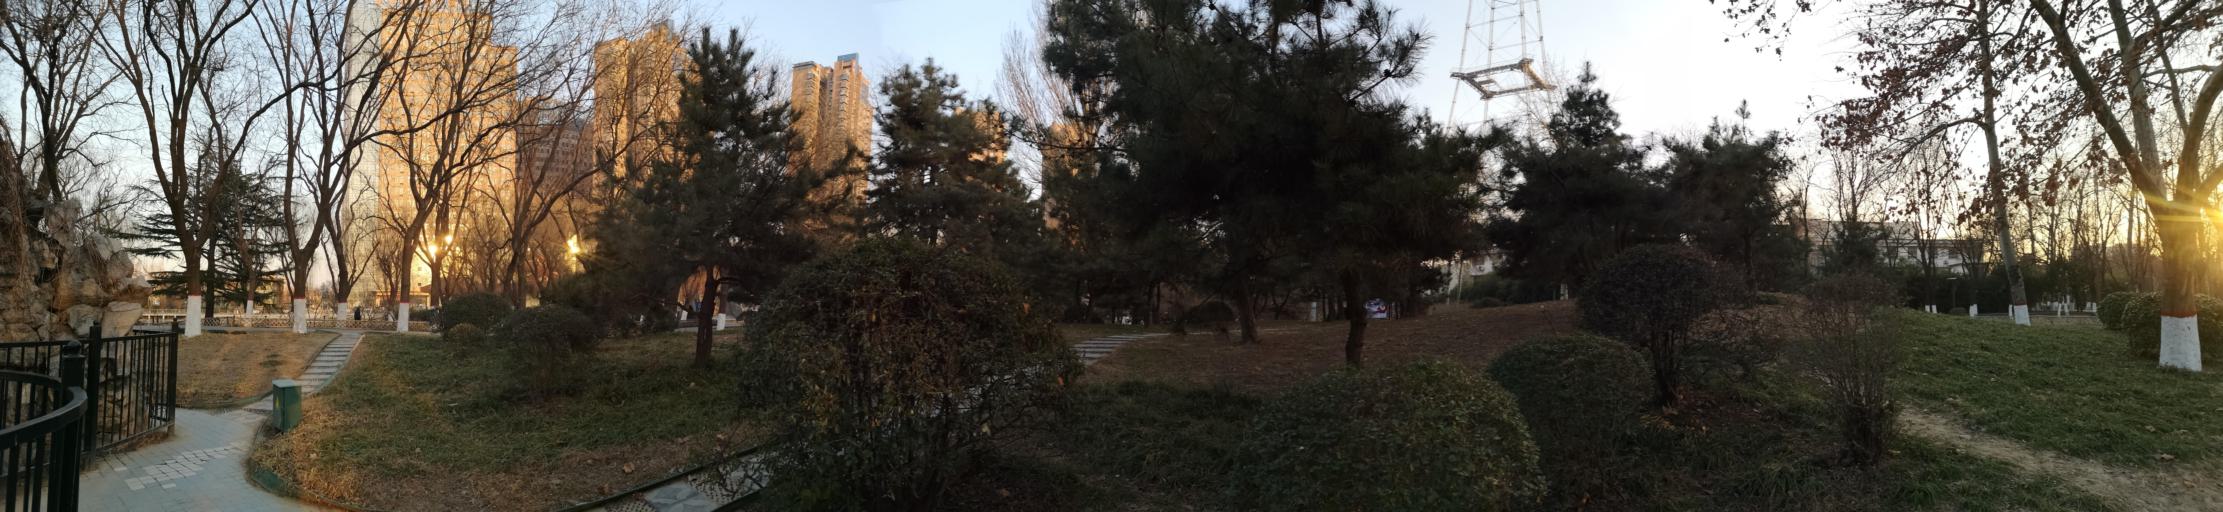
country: CN
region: Henan Sheng
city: Zhongyuanlu
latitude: 35.7740
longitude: 115.0773
